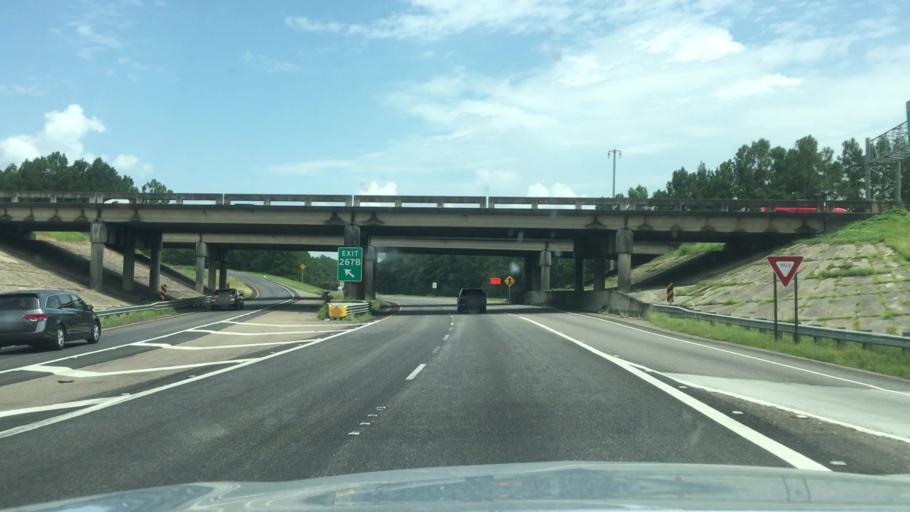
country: US
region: Louisiana
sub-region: Saint Tammany Parish
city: Slidell
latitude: 30.3053
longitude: -89.7404
